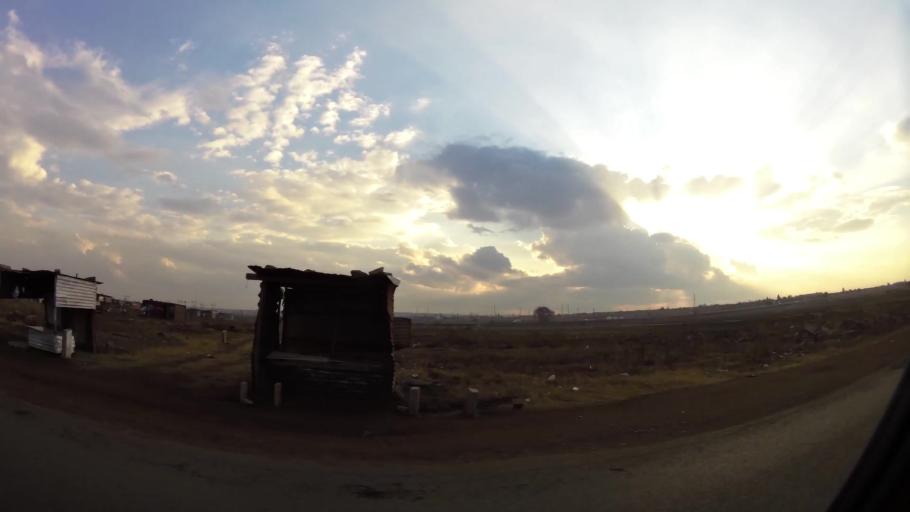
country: ZA
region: Gauteng
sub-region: City of Johannesburg Metropolitan Municipality
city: Orange Farm
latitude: -26.5453
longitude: 27.8333
